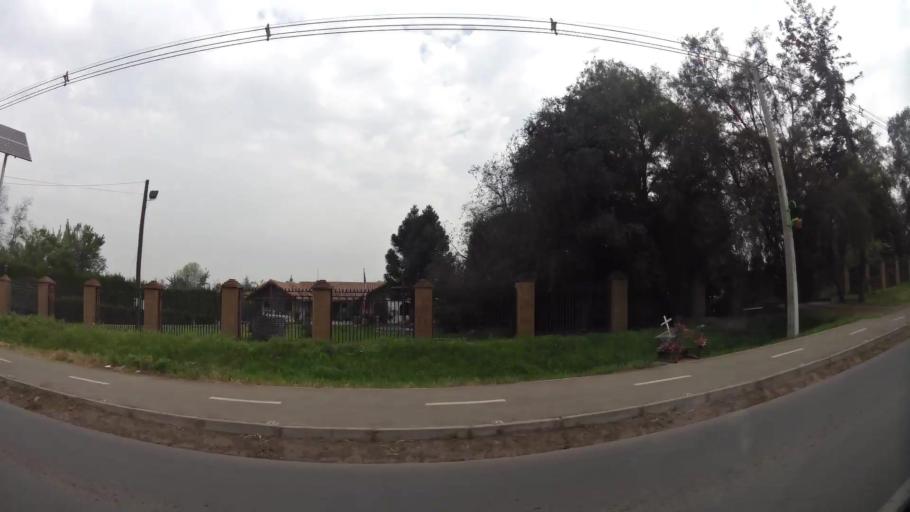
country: CL
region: Santiago Metropolitan
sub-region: Provincia de Chacabuco
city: Chicureo Abajo
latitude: -33.1964
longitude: -70.6783
